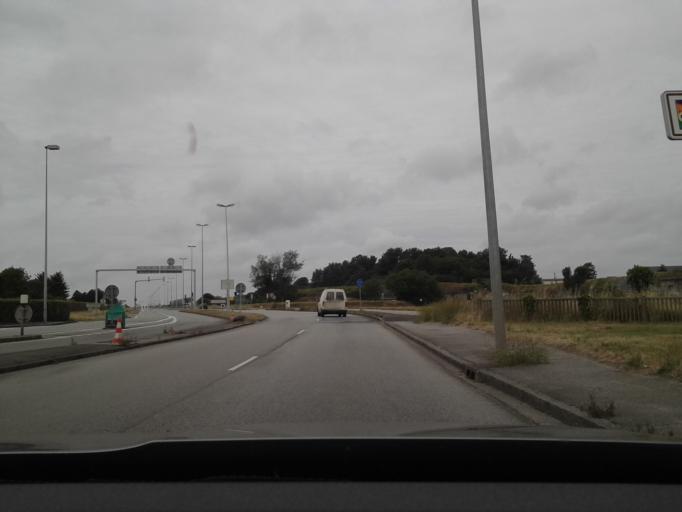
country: FR
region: Lower Normandy
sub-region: Departement de la Manche
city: Equeurdreville-Hainneville
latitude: 49.6476
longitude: -1.6430
